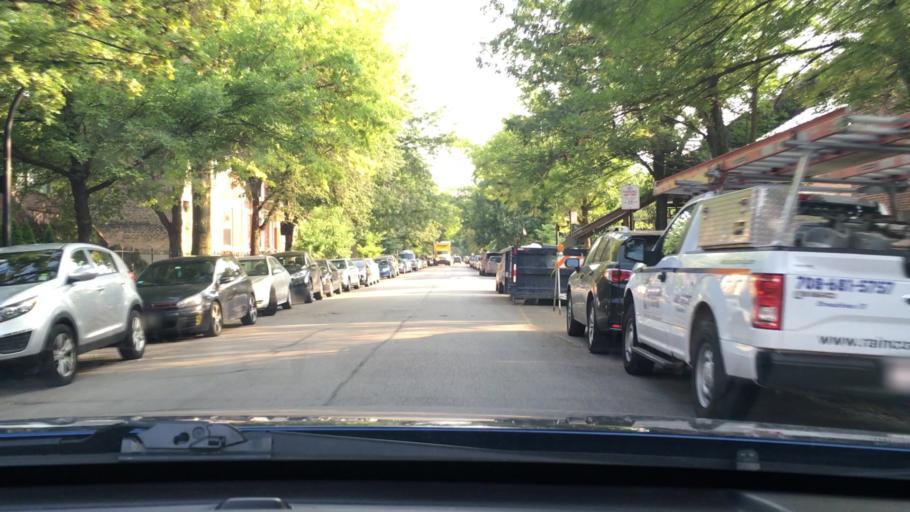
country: US
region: Illinois
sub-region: Cook County
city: Chicago
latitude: 41.8716
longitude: -87.6641
